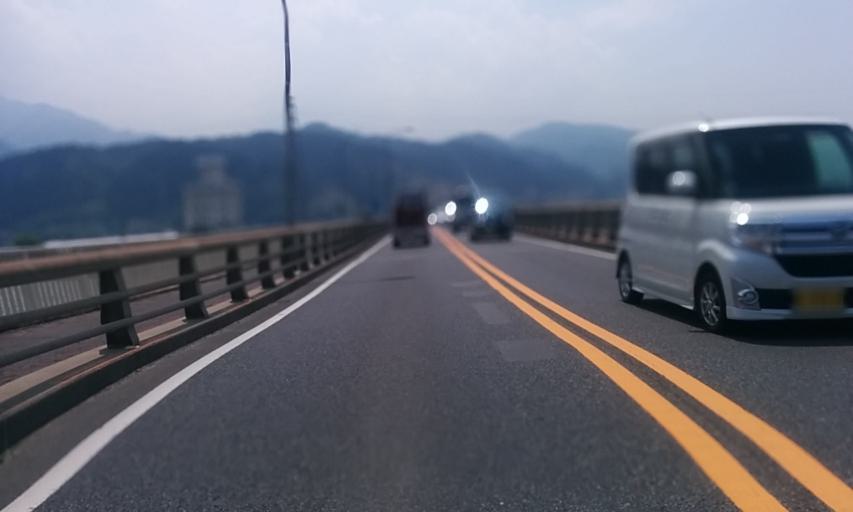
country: JP
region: Ehime
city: Saijo
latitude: 33.9041
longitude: 133.1848
